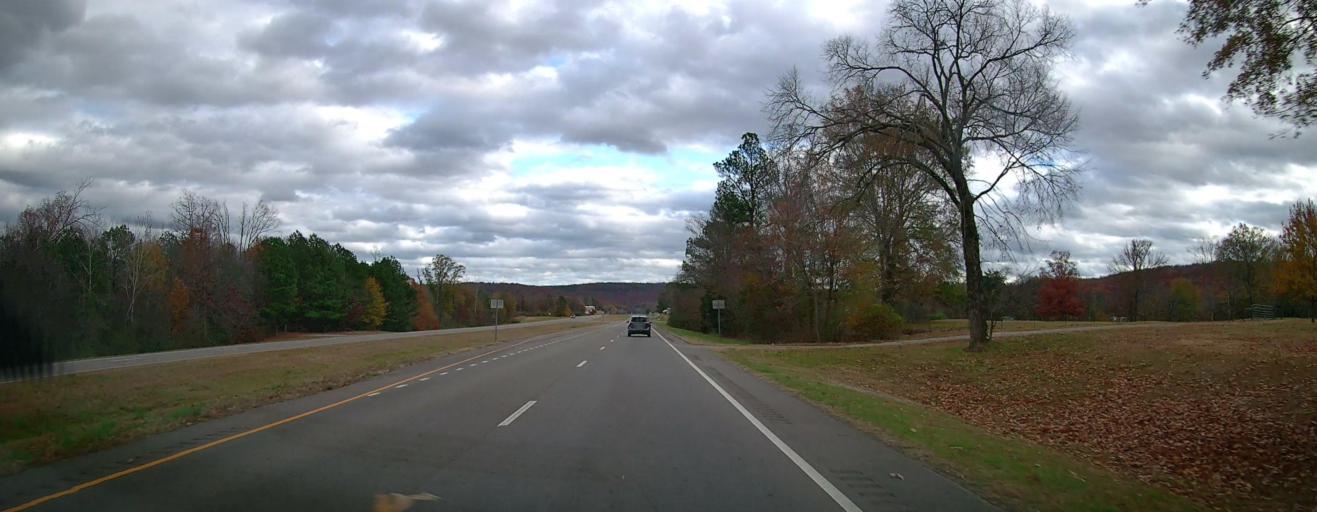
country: US
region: Alabama
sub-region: Morgan County
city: Danville
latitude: 34.3399
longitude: -87.0250
